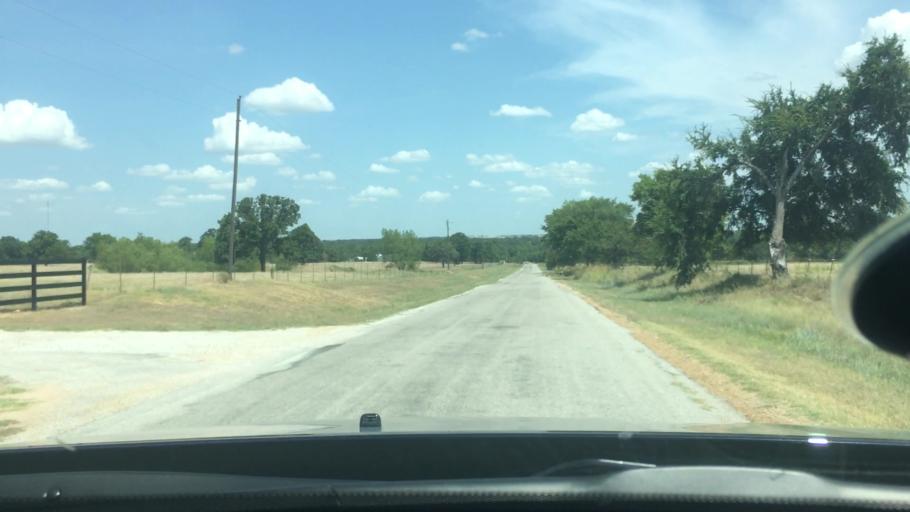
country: US
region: Oklahoma
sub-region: Carter County
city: Ardmore
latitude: 34.0486
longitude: -97.1957
